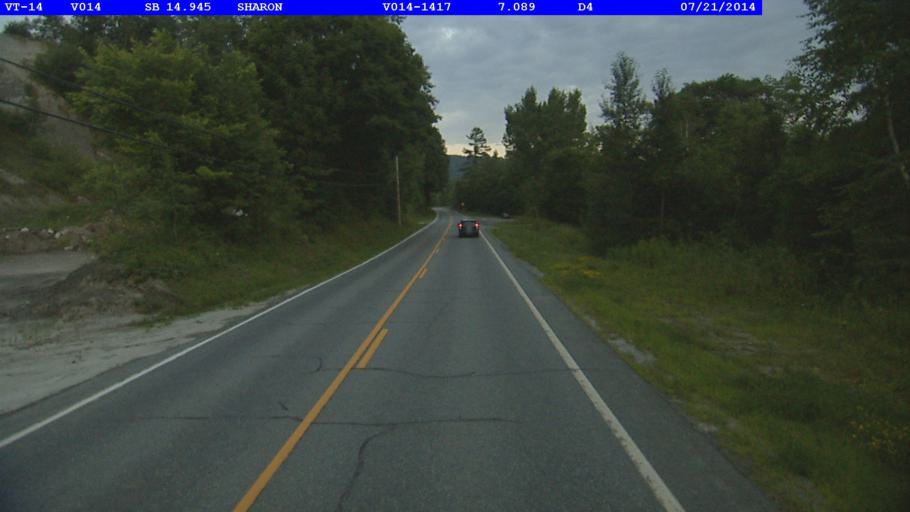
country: US
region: Vermont
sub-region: Windsor County
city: Woodstock
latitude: 43.7905
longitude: -72.4895
